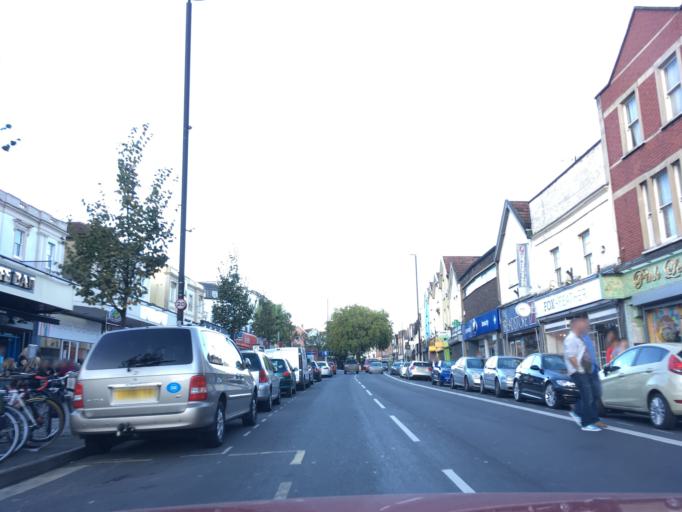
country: GB
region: England
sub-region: Bristol
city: Bristol
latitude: 51.4712
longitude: -2.5929
